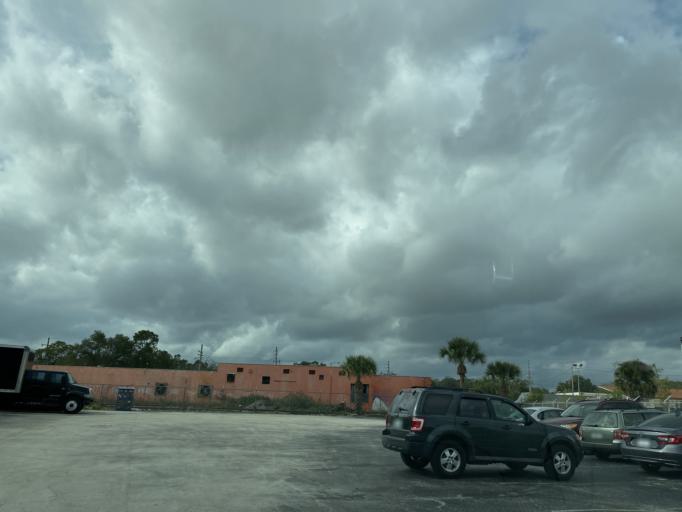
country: US
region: Florida
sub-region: Orange County
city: Orlando
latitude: 28.5518
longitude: -81.3953
